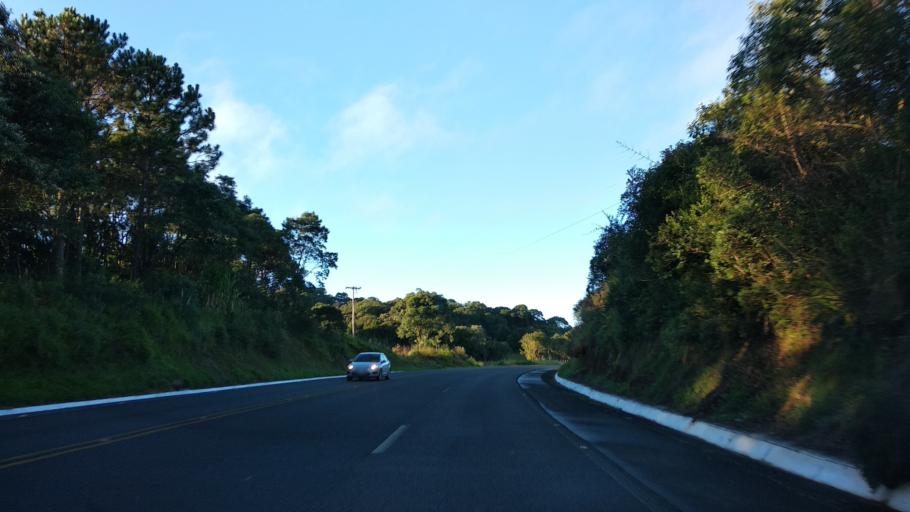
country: BR
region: Santa Catarina
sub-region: Curitibanos
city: Curitibanos
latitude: -27.6092
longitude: -50.7180
